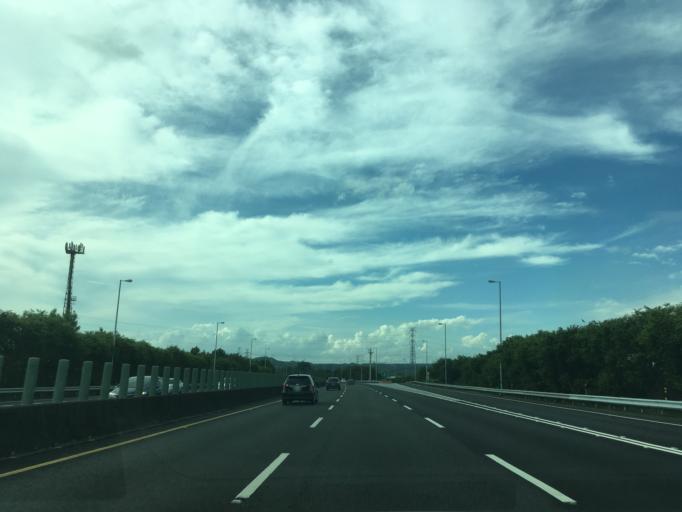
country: TW
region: Taiwan
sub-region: Chiayi
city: Jiayi Shi
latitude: 23.4958
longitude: 120.4940
